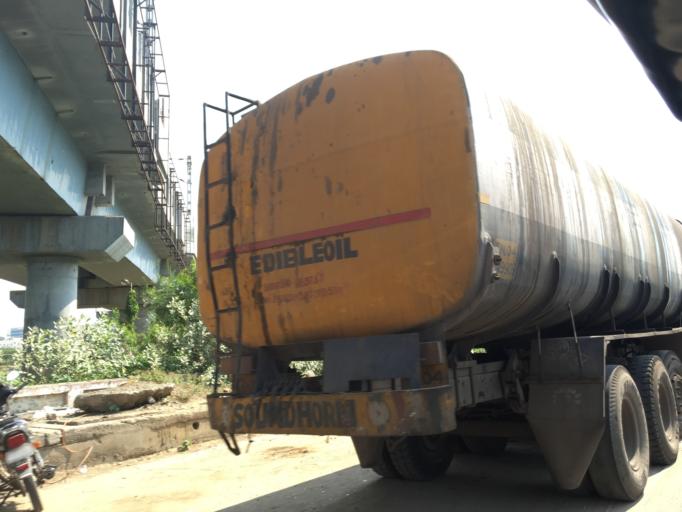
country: IN
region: Tamil Nadu
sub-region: Kancheepuram
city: Perungudi
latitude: 12.9808
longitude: 80.2479
